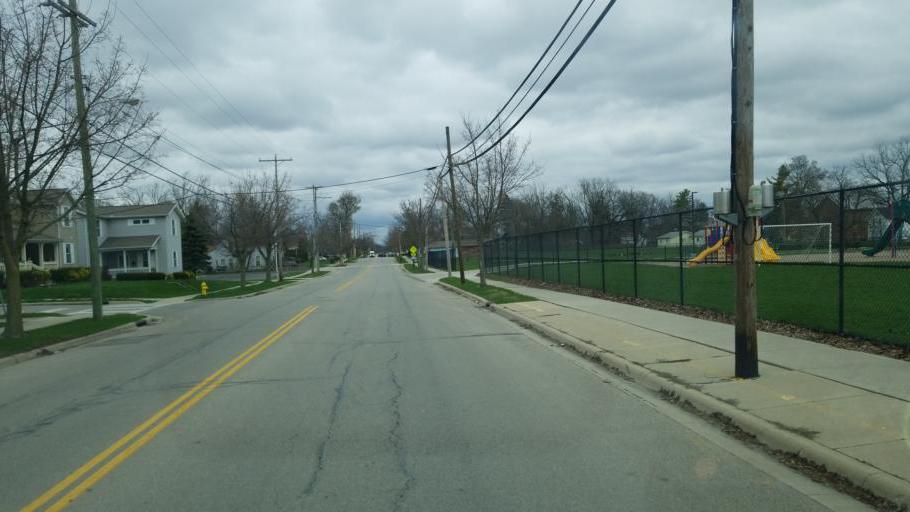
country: US
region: Ohio
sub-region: Delaware County
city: Delaware
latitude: 40.2930
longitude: -83.0735
